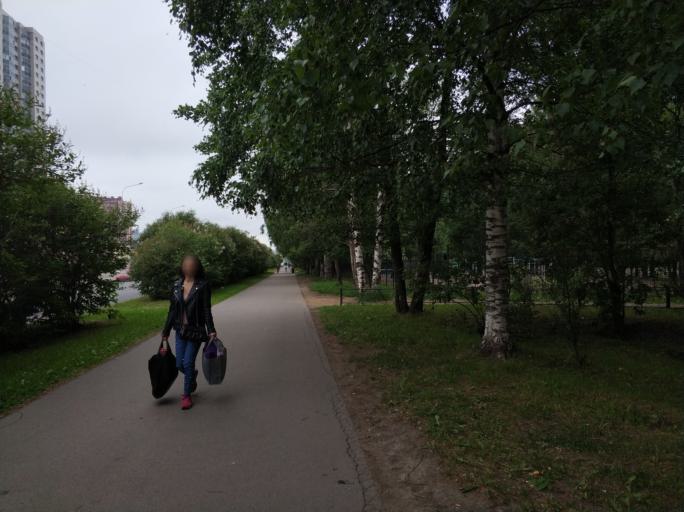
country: RU
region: St.-Petersburg
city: Grazhdanka
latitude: 60.0344
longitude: 30.4093
